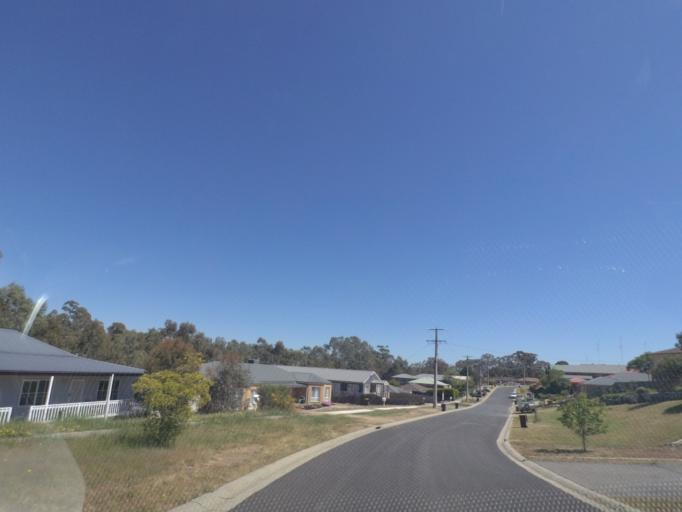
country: AU
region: Victoria
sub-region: Whittlesea
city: Whittlesea
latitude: -37.2096
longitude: 145.0628
